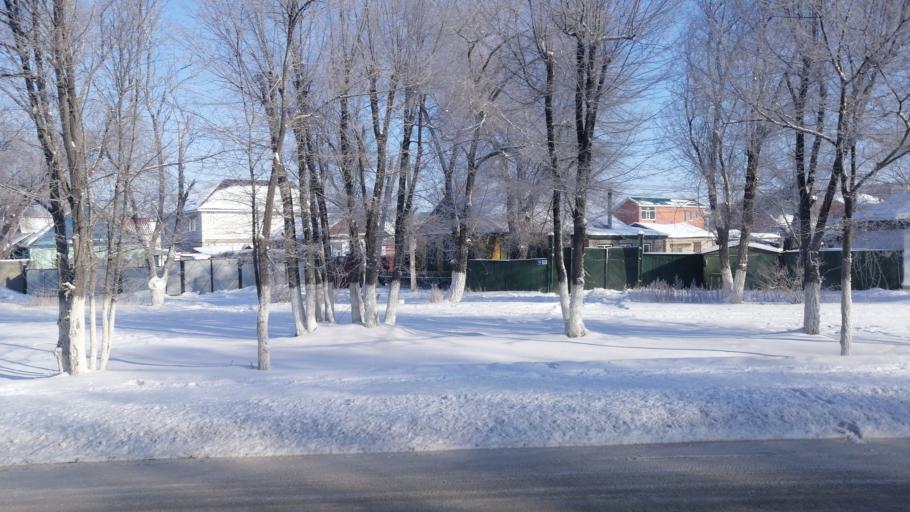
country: KZ
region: Aqtoebe
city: Aqtobe
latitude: 50.2862
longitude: 57.2111
